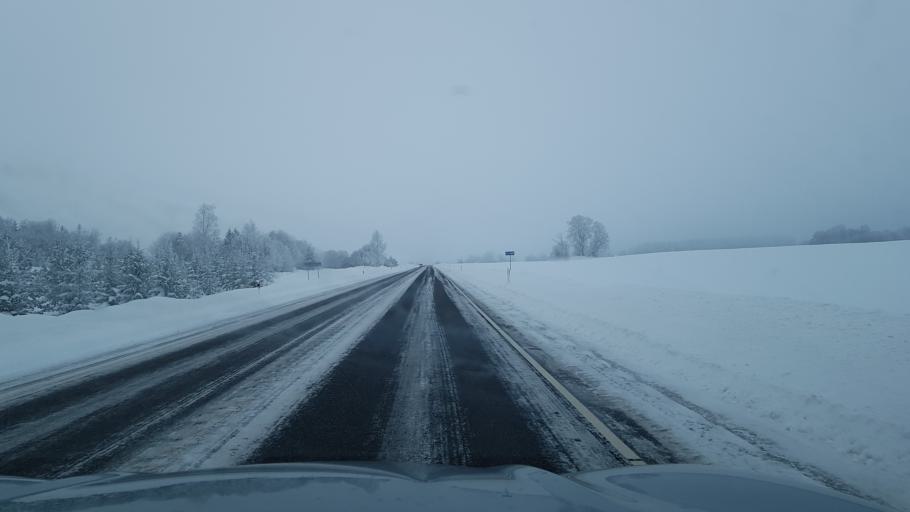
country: EE
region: Ida-Virumaa
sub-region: Johvi vald
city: Johvi
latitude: 59.2455
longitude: 27.3665
